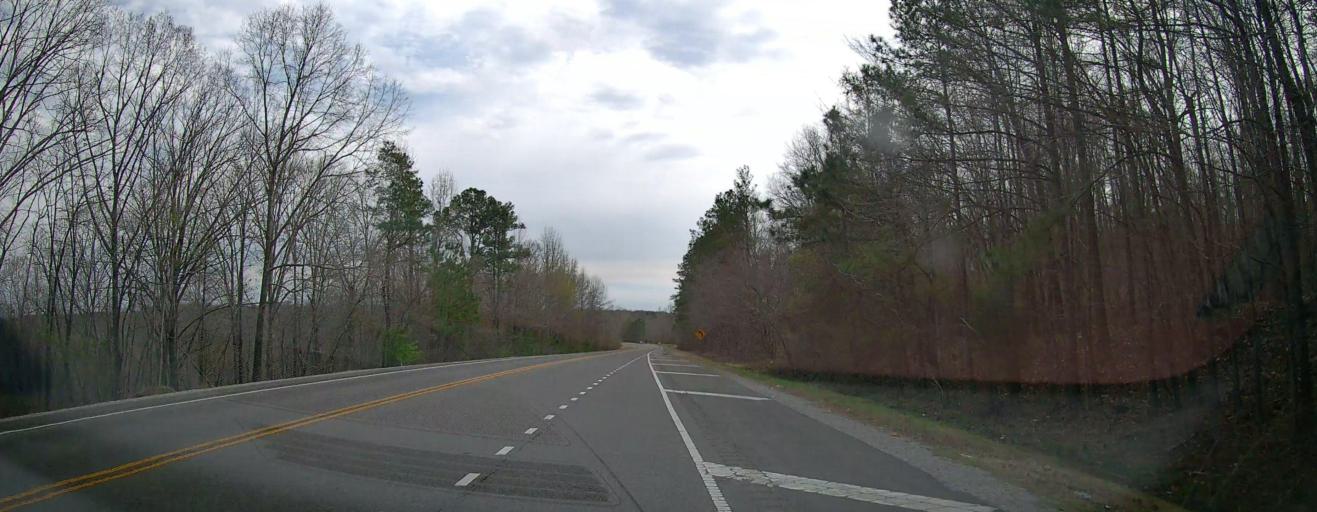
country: US
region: Alabama
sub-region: Marion County
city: Hamilton
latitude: 34.0540
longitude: -87.9659
